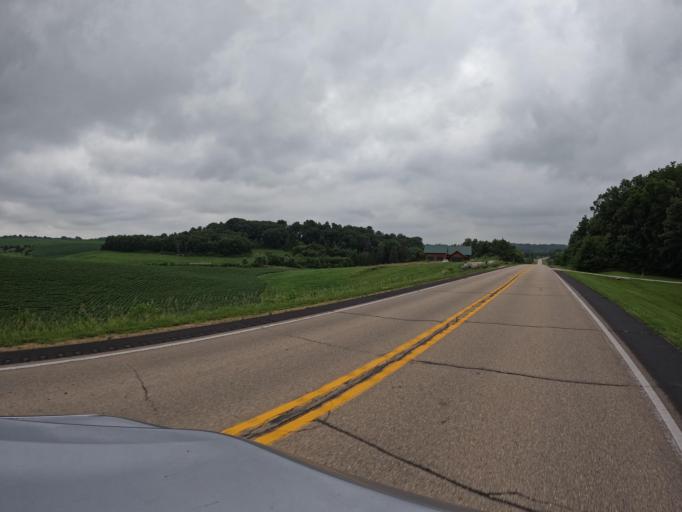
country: US
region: Illinois
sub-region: Carroll County
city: Savanna
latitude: 42.0058
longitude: -90.1845
